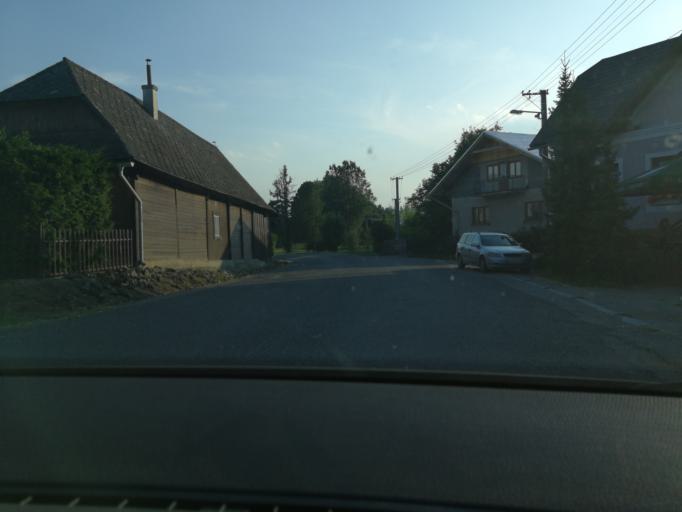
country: SK
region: Zilinsky
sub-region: Okres Liptovsky Mikulas
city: Liptovsky Mikulas
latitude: 49.1649
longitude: 19.5414
